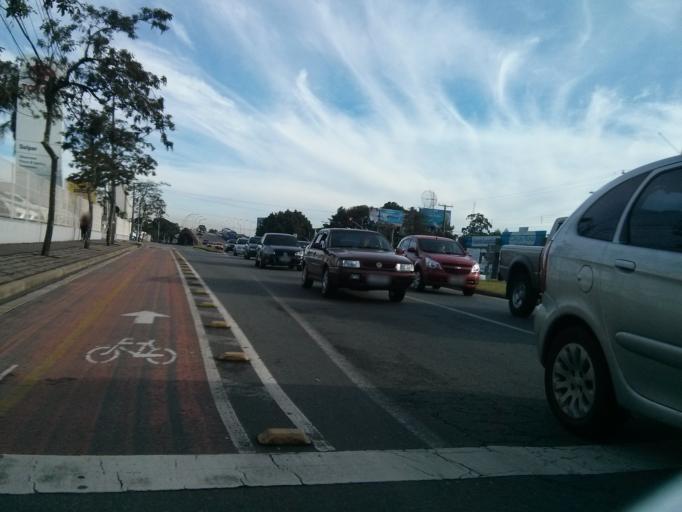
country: BR
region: Parana
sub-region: Curitiba
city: Curitiba
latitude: -25.4713
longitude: -49.2524
